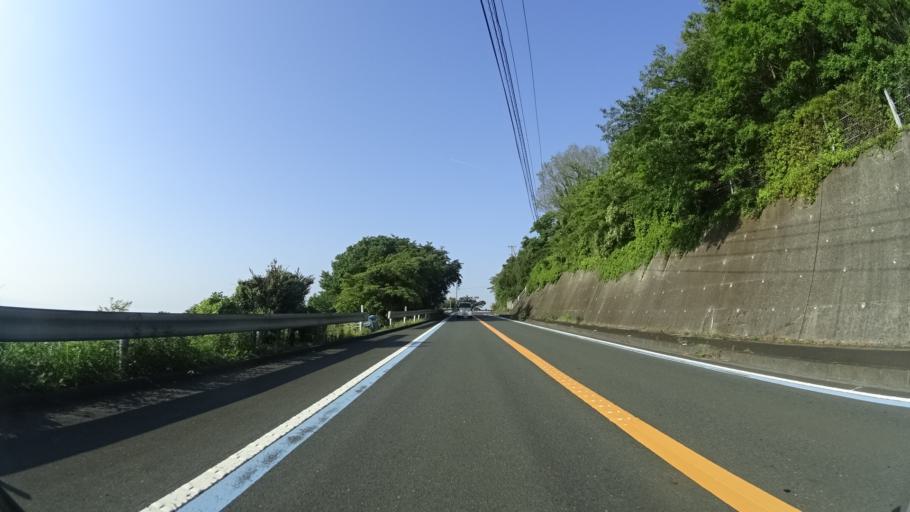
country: JP
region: Ehime
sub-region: Nishiuwa-gun
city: Ikata-cho
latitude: 33.3998
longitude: 132.1652
